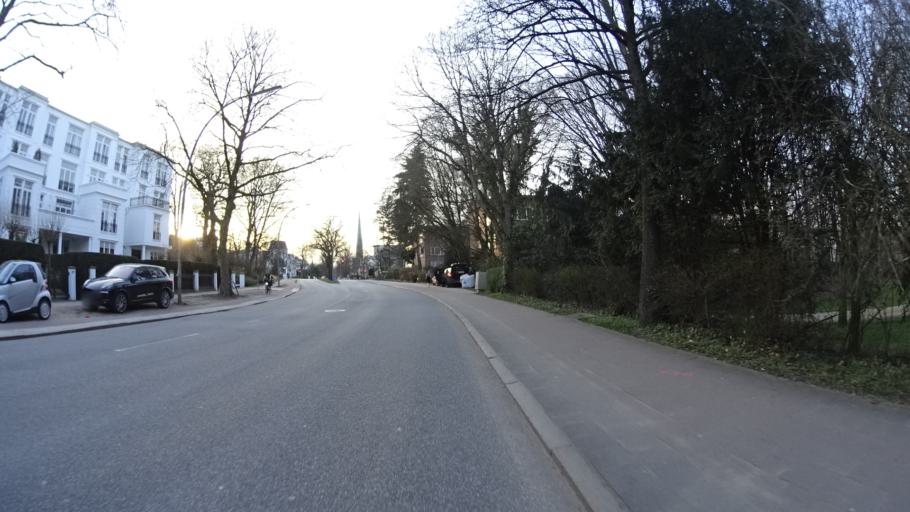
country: DE
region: Hamburg
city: Hamburg-Nord
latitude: 53.5777
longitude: 9.9960
